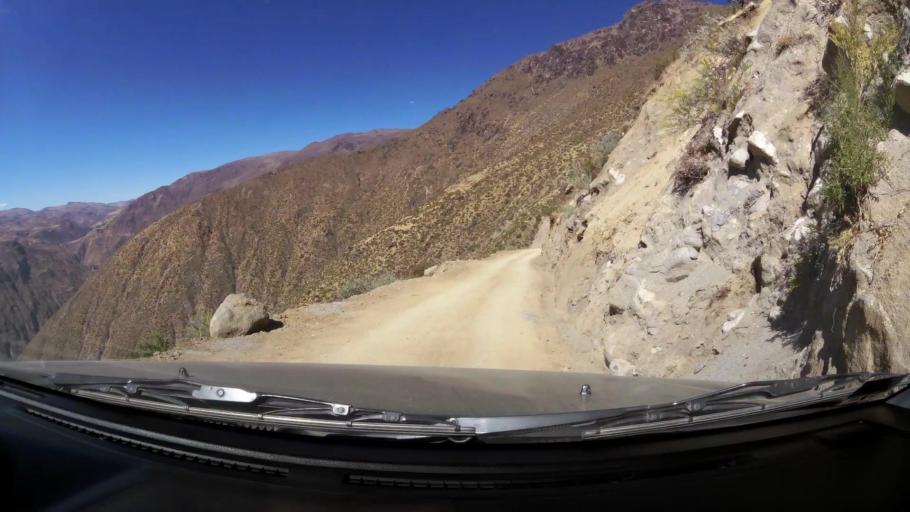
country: PE
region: Huancavelica
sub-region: Huaytara
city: Quito-Arma
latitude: -13.6185
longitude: -75.3524
